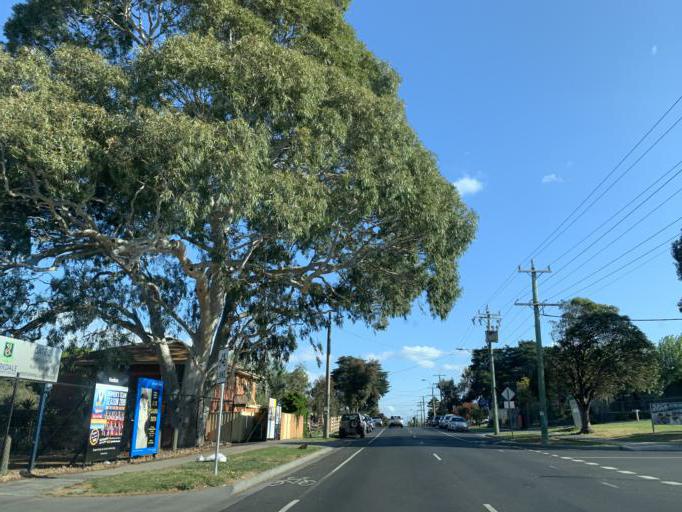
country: AU
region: Victoria
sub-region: Kingston
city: Mordialloc
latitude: -37.9906
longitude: 145.0932
